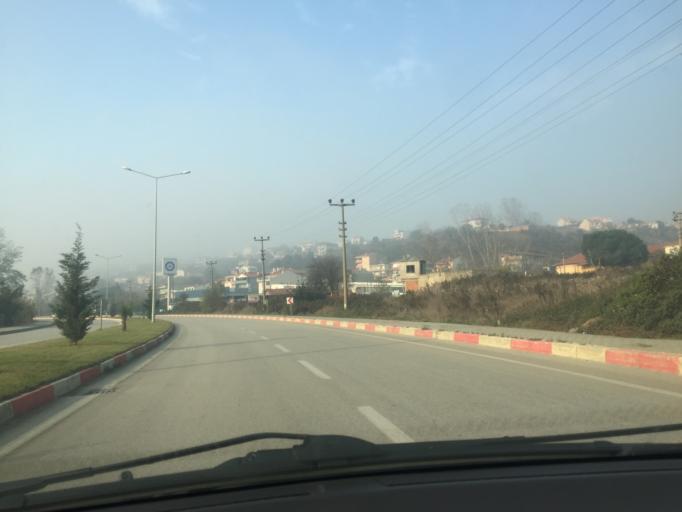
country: TR
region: Canakkale
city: Can
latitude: 40.0363
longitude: 27.0676
